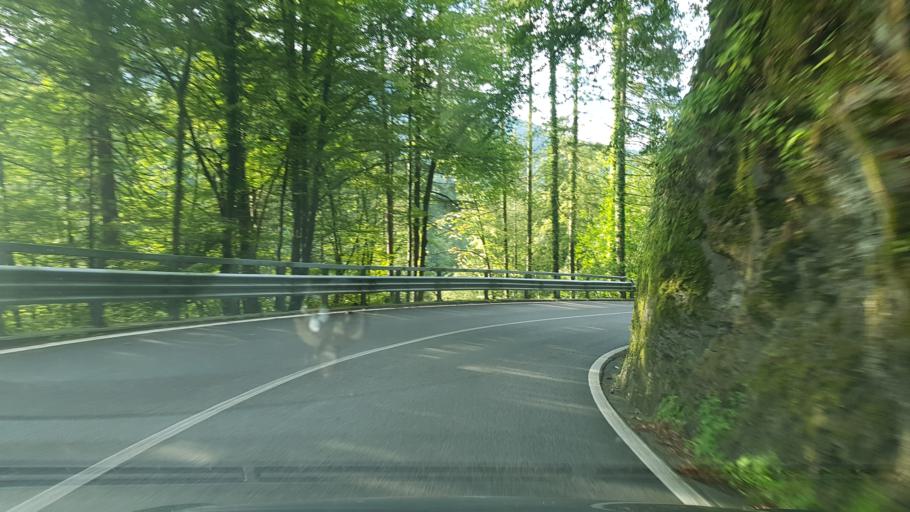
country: IT
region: Friuli Venezia Giulia
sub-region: Provincia di Udine
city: Comeglians
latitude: 46.5254
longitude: 12.8695
